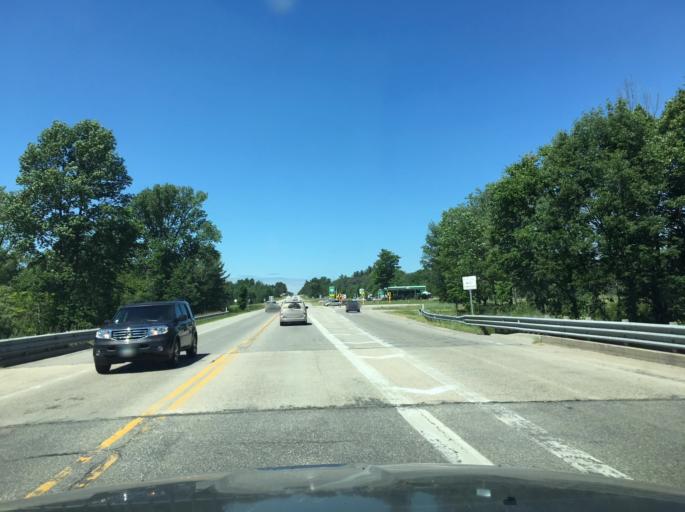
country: US
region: Michigan
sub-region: Osceola County
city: Reed City
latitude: 43.8875
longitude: -85.5300
